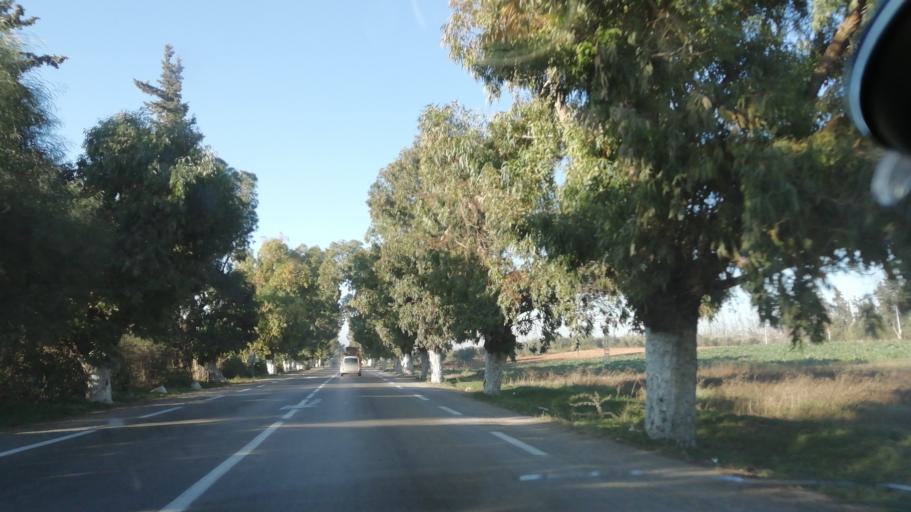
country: DZ
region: Tlemcen
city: Remchi
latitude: 35.0708
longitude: -1.4631
